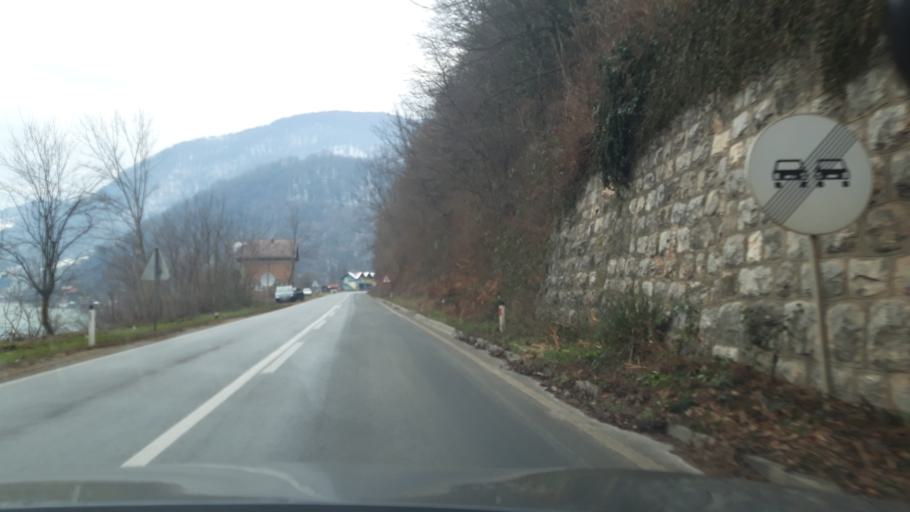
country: RS
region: Central Serbia
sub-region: Macvanski Okrug
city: Mali Zvornik
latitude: 44.3231
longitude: 19.1273
